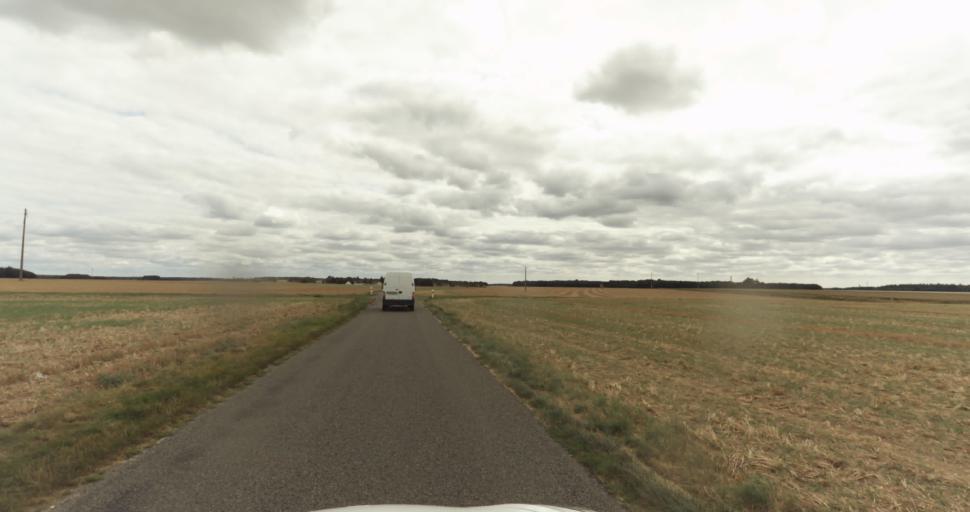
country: FR
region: Haute-Normandie
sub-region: Departement de l'Eure
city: Saint-Germain-sur-Avre
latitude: 48.8063
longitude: 1.2515
